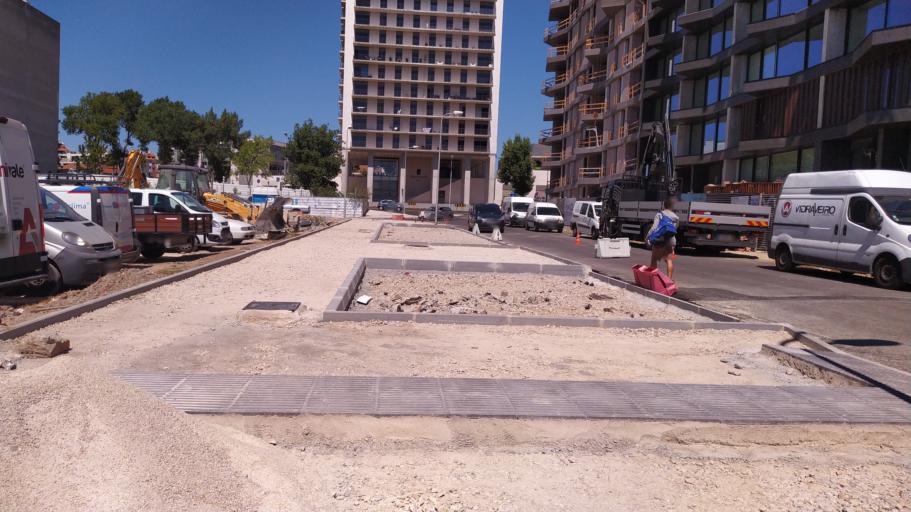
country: PT
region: Aveiro
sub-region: Aveiro
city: Aveiro
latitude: 40.6402
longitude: -8.6432
